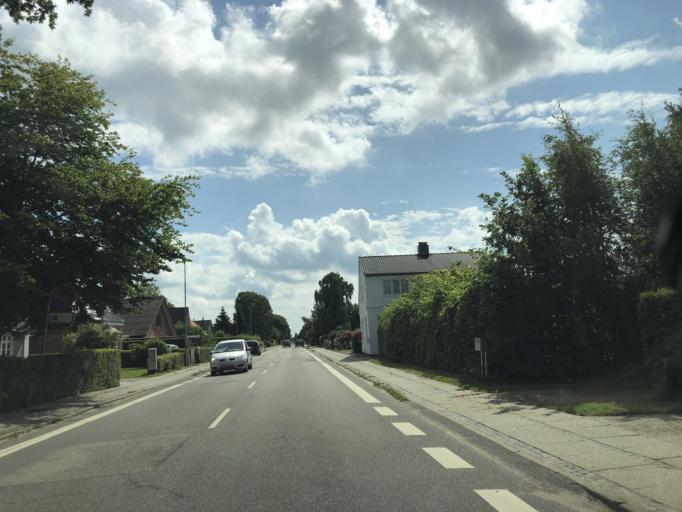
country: DK
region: Central Jutland
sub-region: Ikast-Brande Kommune
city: Brande
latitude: 55.9418
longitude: 9.1384
